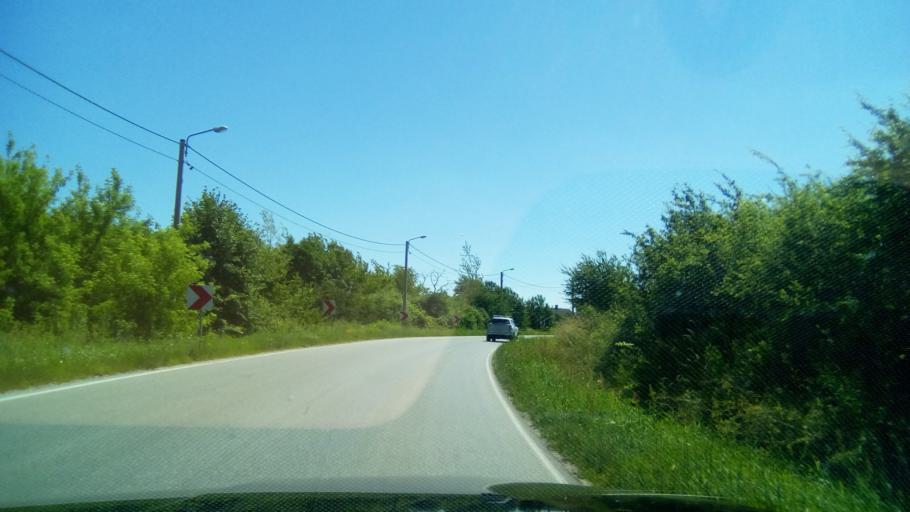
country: PL
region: Masovian Voivodeship
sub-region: Powiat radomski
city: Jedlinsk
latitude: 51.4504
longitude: 21.0840
